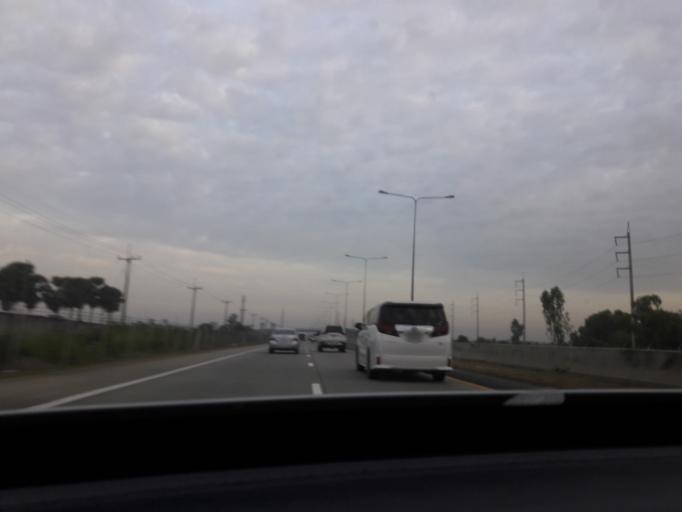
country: TH
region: Pathum Thani
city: Sam Khok
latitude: 14.0939
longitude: 100.5779
